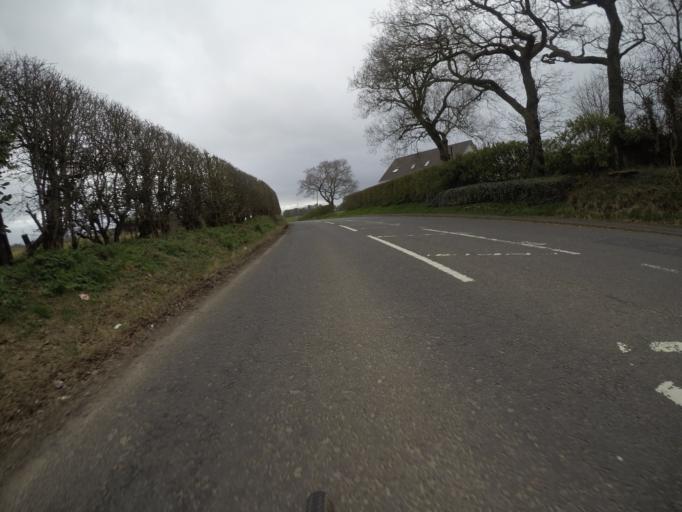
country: GB
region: Scotland
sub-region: East Ayrshire
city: Crosshouse
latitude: 55.6123
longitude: -4.5608
